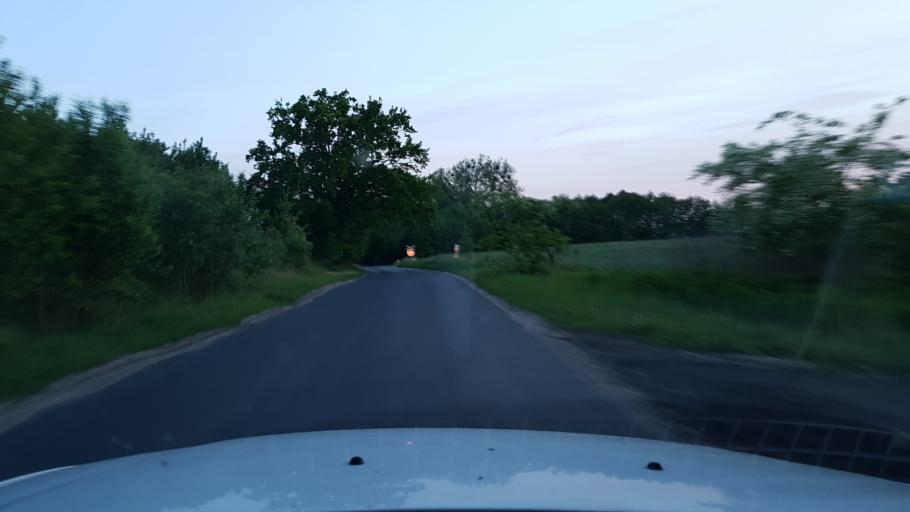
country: PL
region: West Pomeranian Voivodeship
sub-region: Powiat goleniowski
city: Goleniow
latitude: 53.5624
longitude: 14.8584
